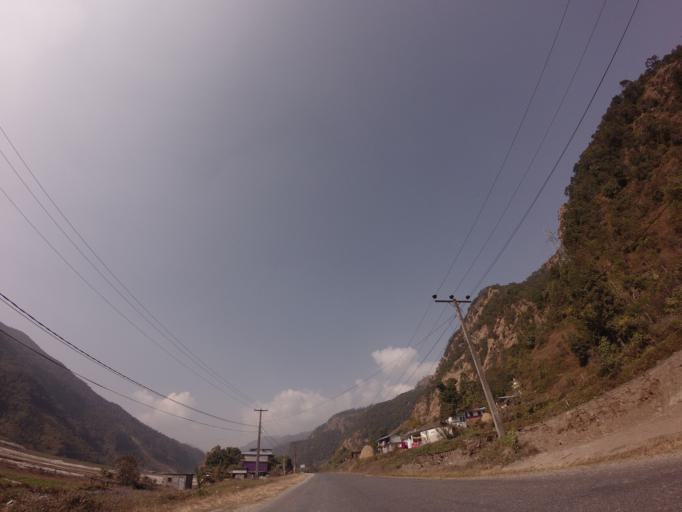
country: NP
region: Western Region
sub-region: Gandaki Zone
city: Pokhara
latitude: 28.2882
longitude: 83.8966
